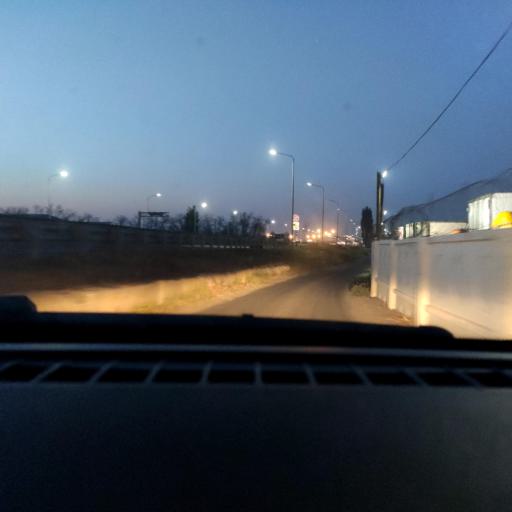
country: RU
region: Voronezj
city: Somovo
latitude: 51.6758
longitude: 39.3006
